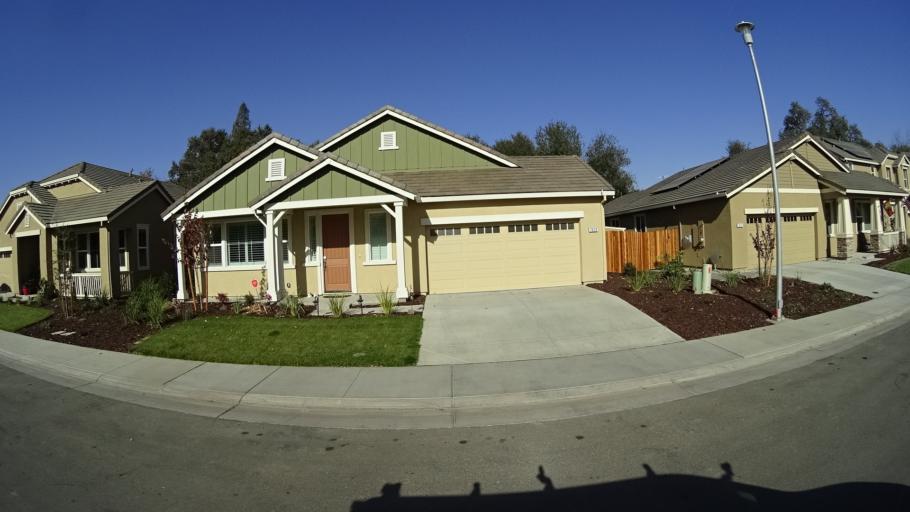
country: US
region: California
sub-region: Sacramento County
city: Citrus Heights
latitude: 38.7062
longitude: -121.2847
